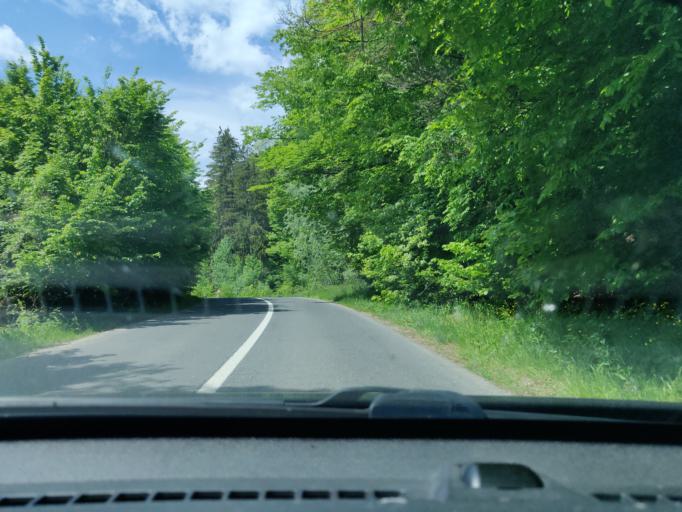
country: RO
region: Vrancea
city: Dragosloveni
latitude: 46.0362
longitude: 26.6995
